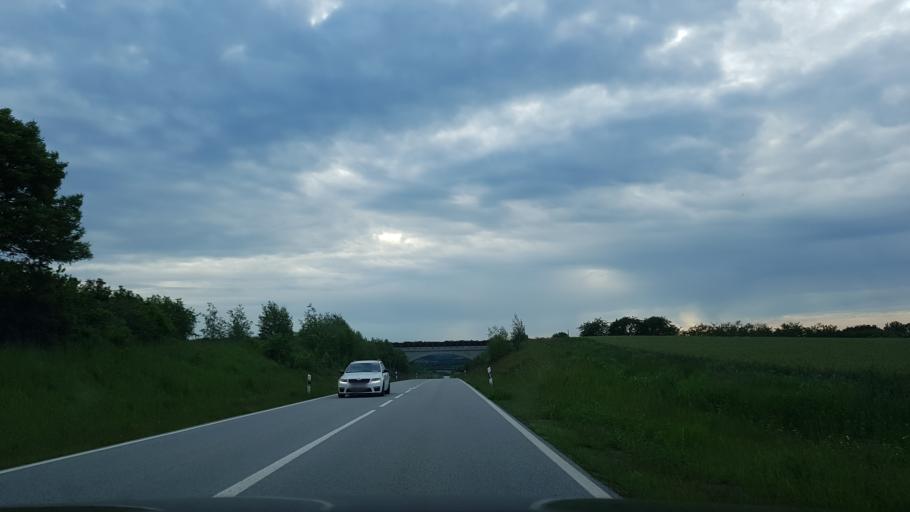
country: DE
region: Saxony
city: Dohma
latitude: 50.8990
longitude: 13.9359
